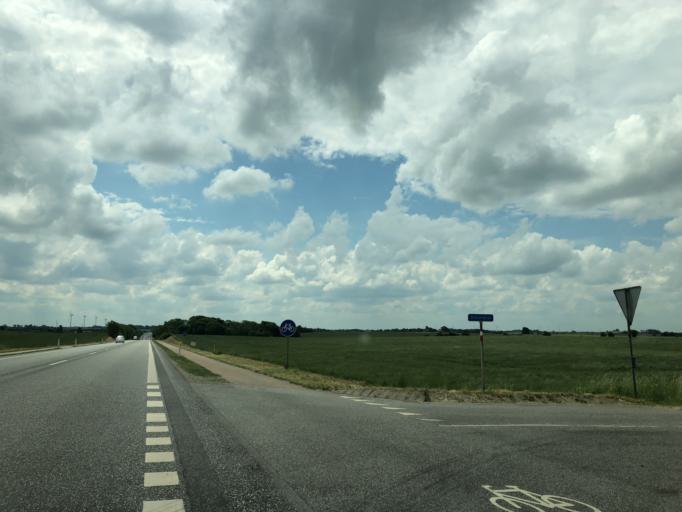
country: DK
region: Central Jutland
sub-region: Struer Kommune
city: Struer
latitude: 56.4648
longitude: 8.5886
